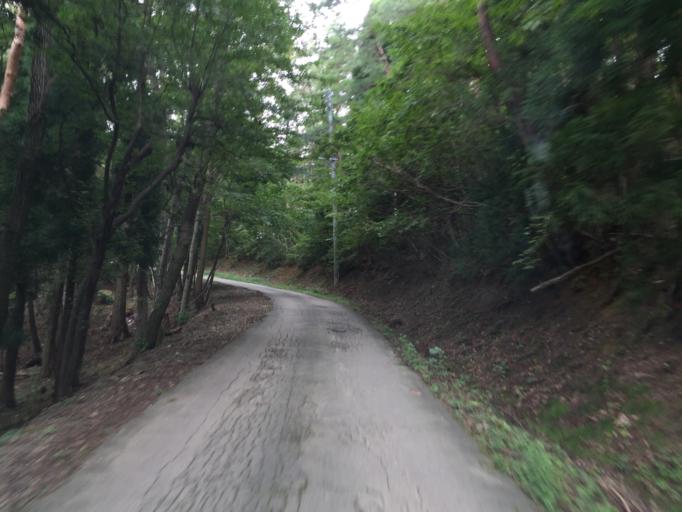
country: JP
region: Fukushima
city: Fukushima-shi
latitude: 37.7747
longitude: 140.4740
